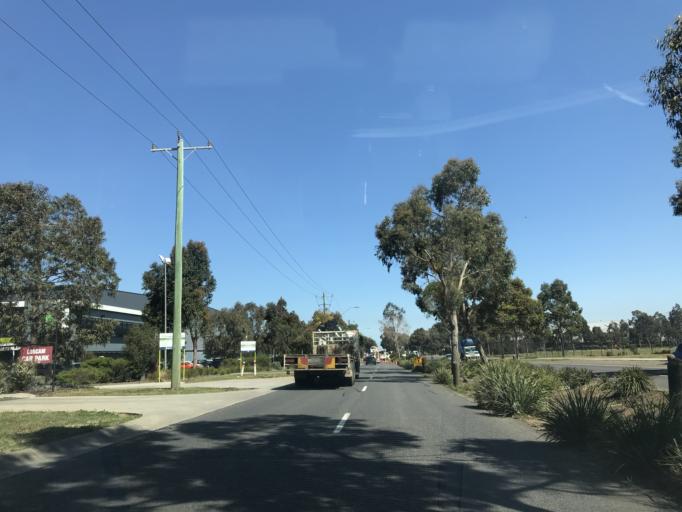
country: AU
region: Victoria
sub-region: Wyndham
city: Truganina
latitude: -37.8148
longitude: 144.7656
